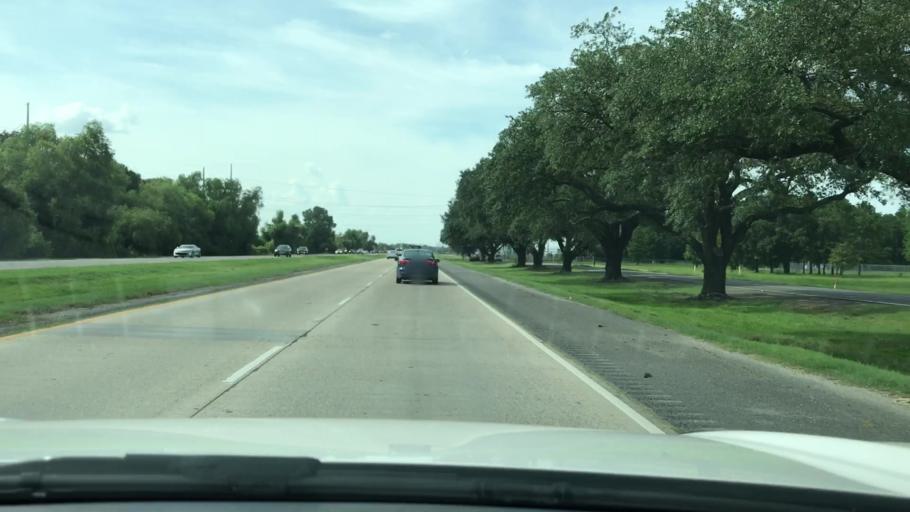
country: US
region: Louisiana
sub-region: West Baton Rouge Parish
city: Addis
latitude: 30.3273
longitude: -91.2546
